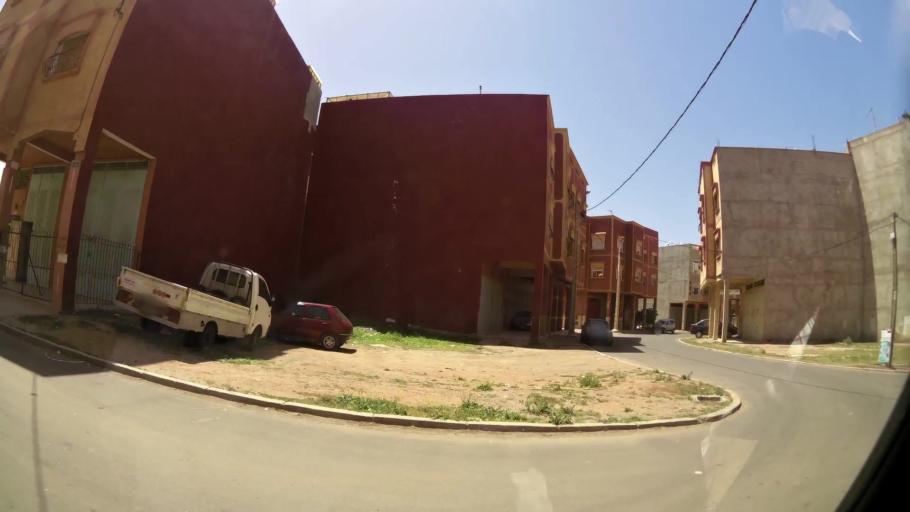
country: MA
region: Souss-Massa-Draa
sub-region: Inezgane-Ait Mellou
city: Inezgane
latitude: 30.3461
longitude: -9.4831
